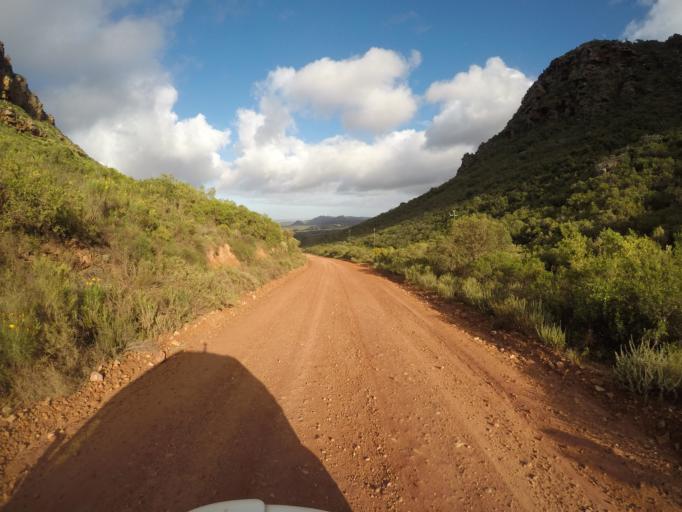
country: ZA
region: Western Cape
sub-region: West Coast District Municipality
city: Clanwilliam
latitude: -32.3403
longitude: 18.7866
